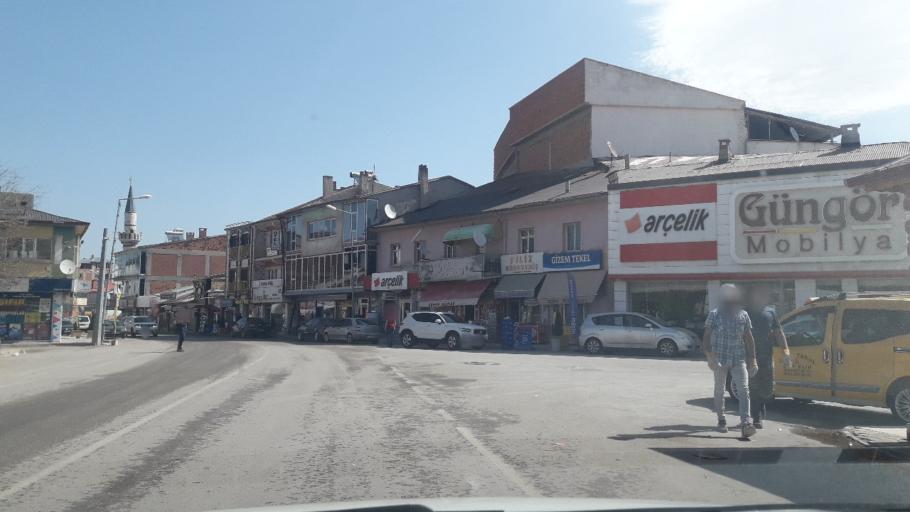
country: TR
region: Sivas
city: Kangal
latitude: 39.2342
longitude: 37.3910
